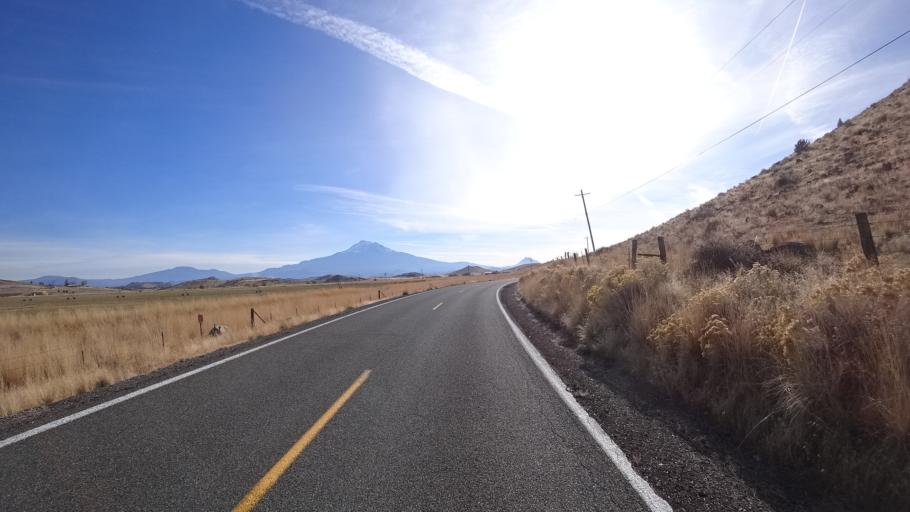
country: US
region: California
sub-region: Siskiyou County
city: Weed
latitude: 41.5369
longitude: -122.5209
